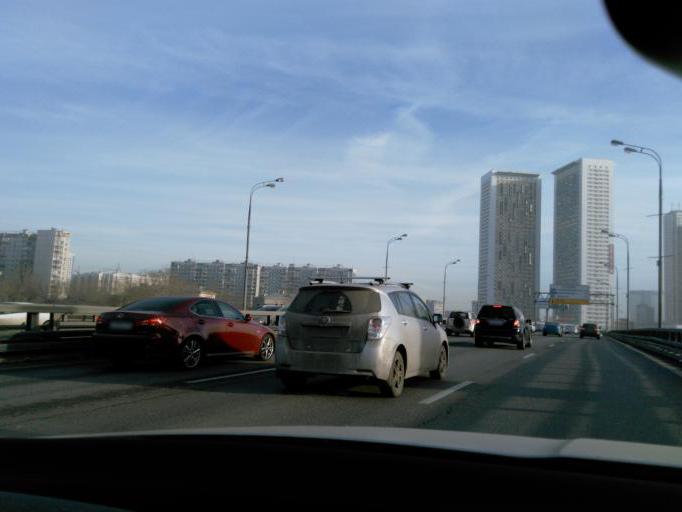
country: RU
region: Moskovskaya
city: Presnenskiy
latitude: 55.7707
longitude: 37.5429
